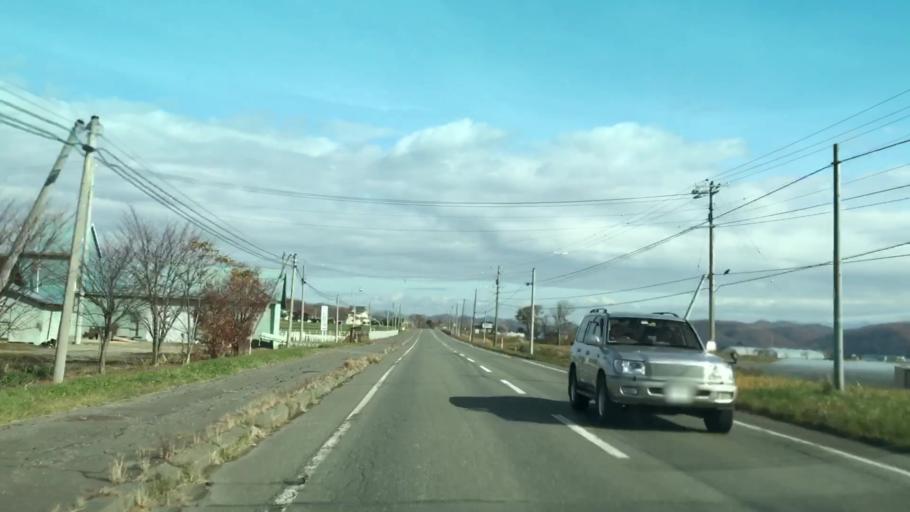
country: JP
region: Hokkaido
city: Shizunai-furukawacho
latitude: 42.5711
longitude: 142.0996
